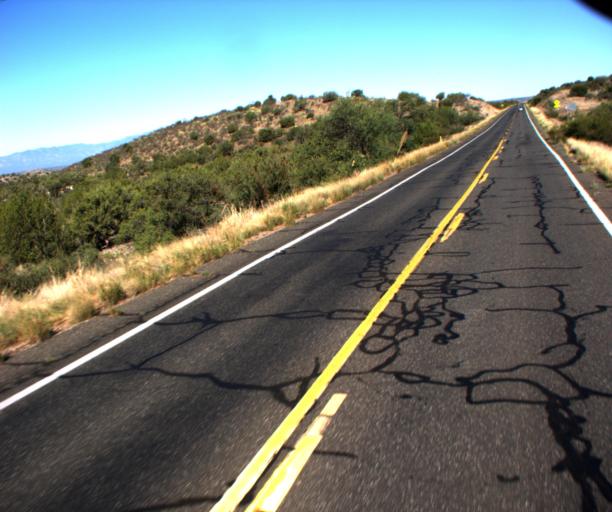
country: US
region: Arizona
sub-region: Yavapai County
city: Lake Montezuma
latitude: 34.6959
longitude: -111.7562
